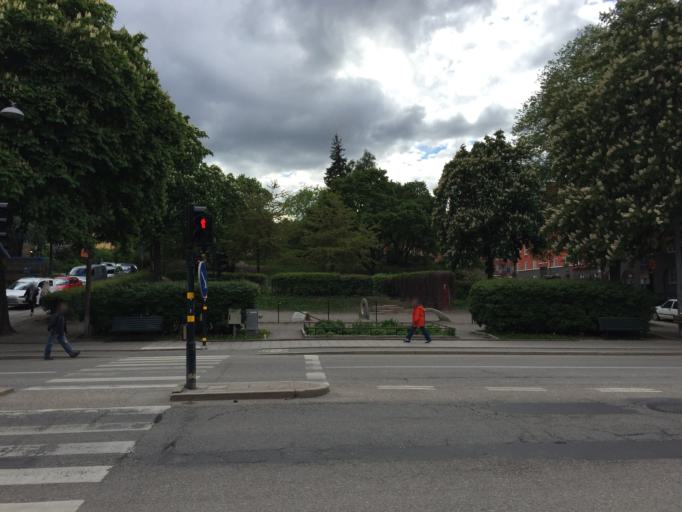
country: SE
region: Stockholm
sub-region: Stockholms Kommun
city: Stockholm
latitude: 59.3442
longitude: 18.0354
